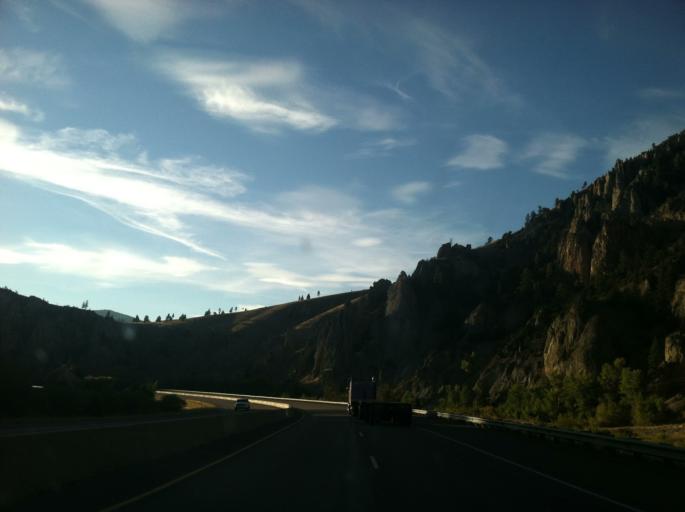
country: US
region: Montana
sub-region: Granite County
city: Philipsburg
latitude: 46.7182
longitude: -113.3122
